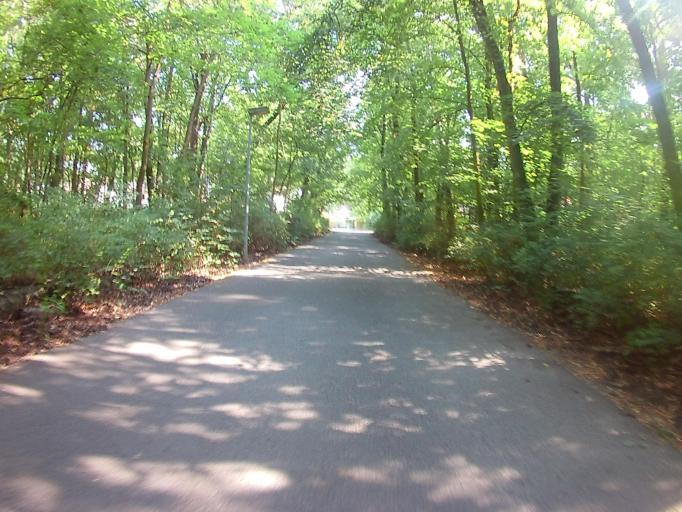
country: DE
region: Berlin
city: Grunau
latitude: 52.4090
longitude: 13.5922
